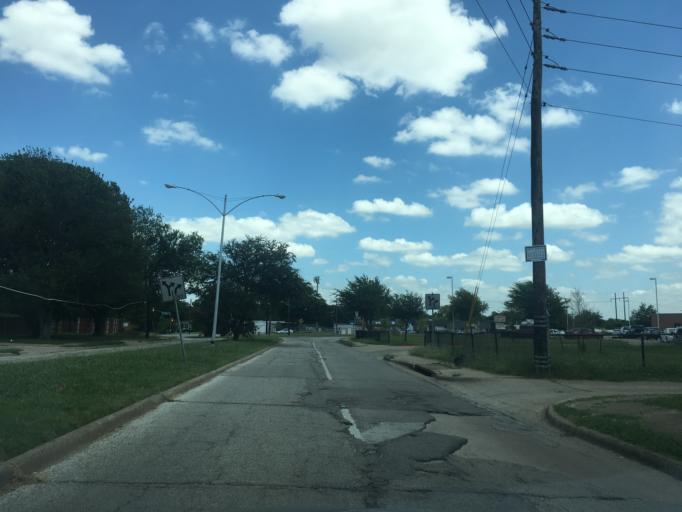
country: US
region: Texas
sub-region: Dallas County
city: Garland
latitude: 32.8348
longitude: -96.6605
